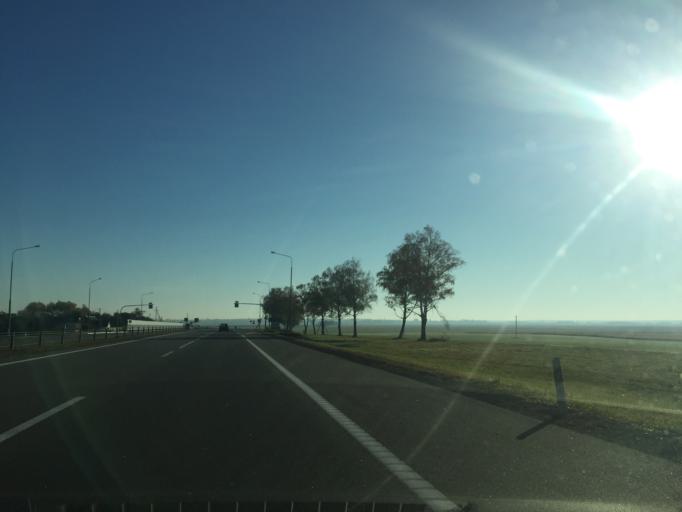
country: BY
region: Minsk
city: Smilavichy
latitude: 53.7616
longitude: 27.9301
